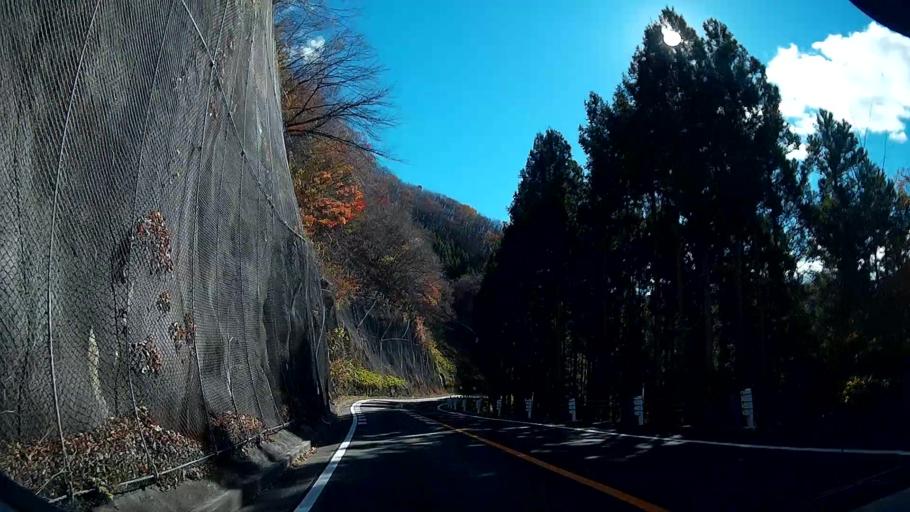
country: JP
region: Yamanashi
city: Uenohara
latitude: 35.7649
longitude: 139.0343
